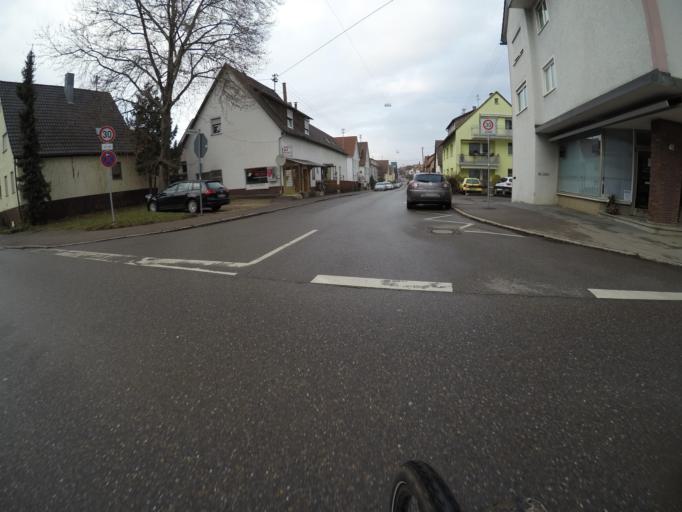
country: DE
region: Baden-Wuerttemberg
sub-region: Regierungsbezirk Stuttgart
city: Filderstadt
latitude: 48.6788
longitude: 9.2215
